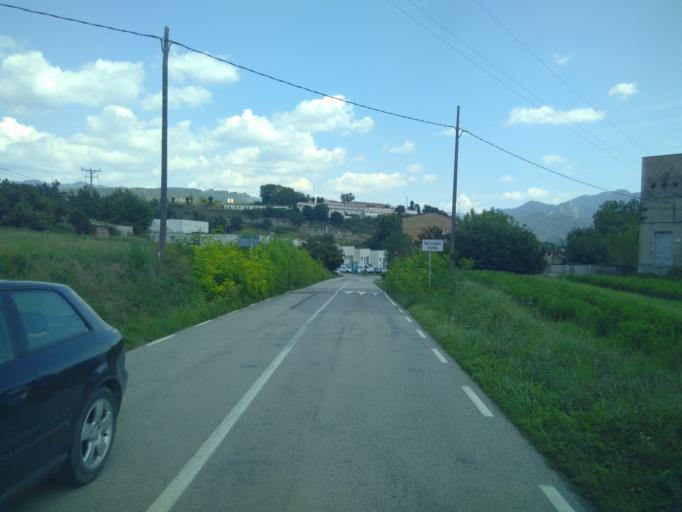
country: ES
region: Catalonia
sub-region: Provincia de Barcelona
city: Montesquiu
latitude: 42.0986
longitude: 2.2019
